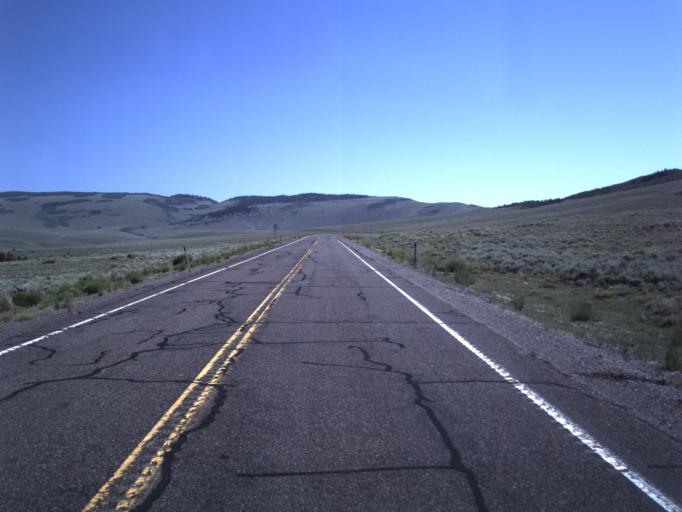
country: US
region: Utah
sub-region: Wayne County
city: Loa
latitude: 38.5555
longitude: -111.5067
